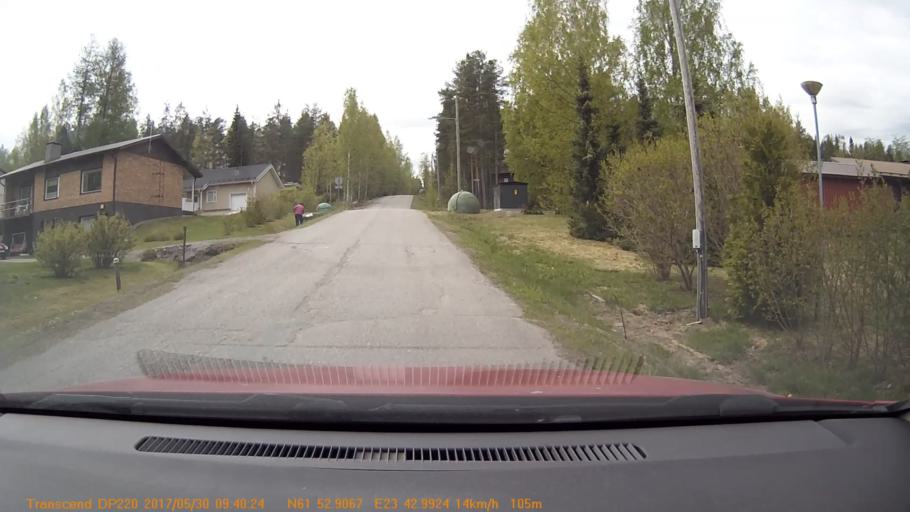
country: FI
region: Pirkanmaa
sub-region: Tampere
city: Kuru
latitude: 61.8817
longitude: 23.7163
